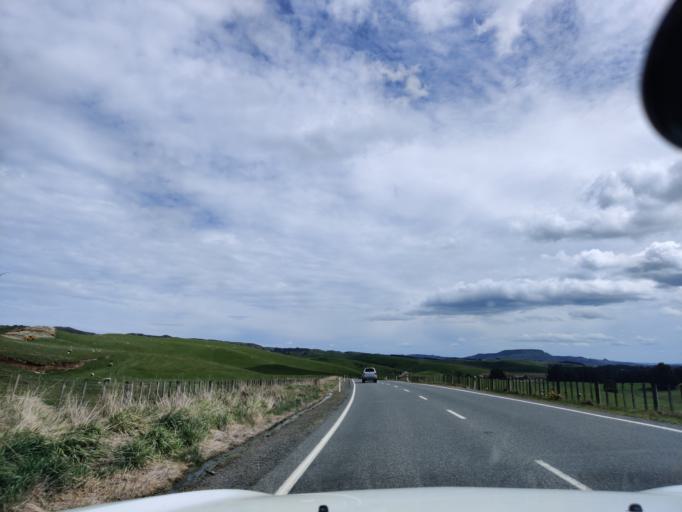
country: NZ
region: Manawatu-Wanganui
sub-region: Ruapehu District
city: Waiouru
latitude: -39.4660
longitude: 175.6570
